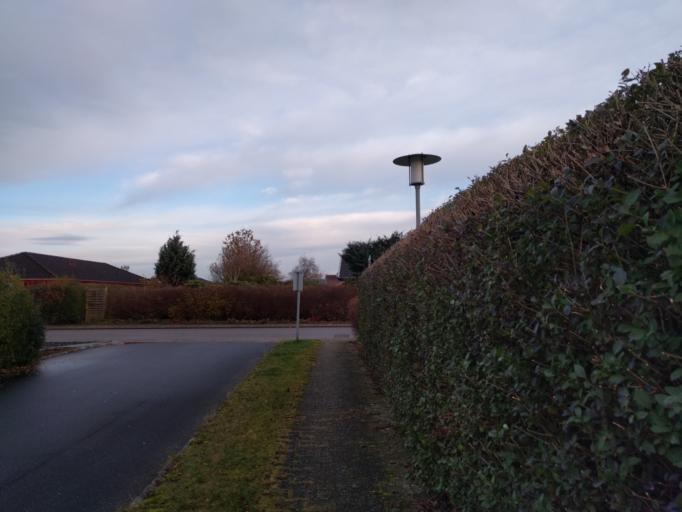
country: DK
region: South Denmark
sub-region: Fredericia Kommune
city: Snoghoj
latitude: 55.5375
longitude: 9.7286
